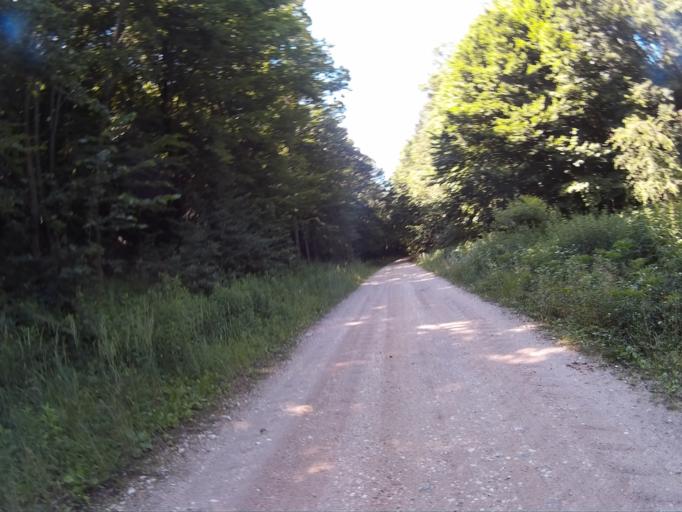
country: HU
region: Veszprem
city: Urkut
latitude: 47.1030
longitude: 17.6646
